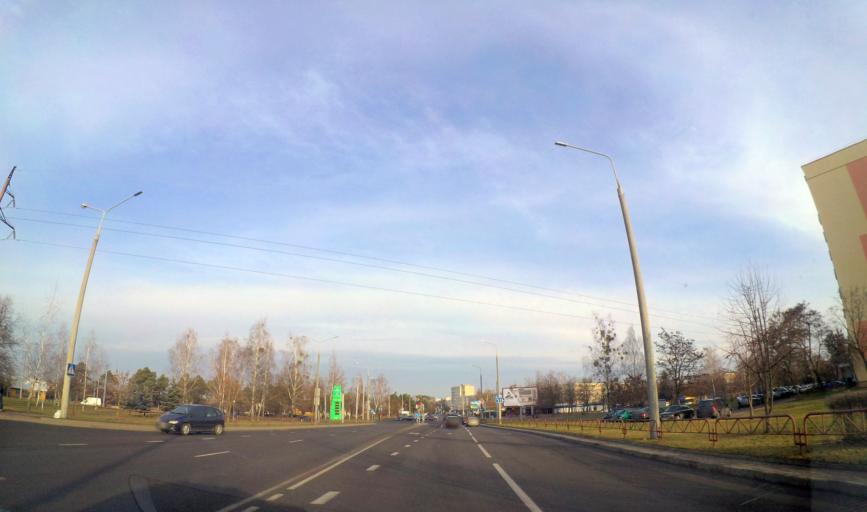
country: BY
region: Grodnenskaya
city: Hrodna
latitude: 53.6651
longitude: 23.7852
